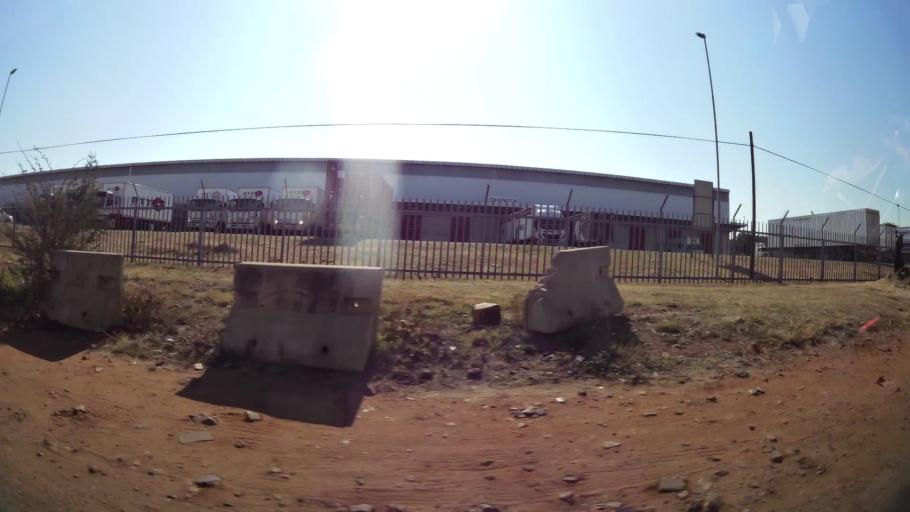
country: ZA
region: Gauteng
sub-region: Ekurhuleni Metropolitan Municipality
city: Boksburg
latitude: -26.1660
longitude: 28.2368
